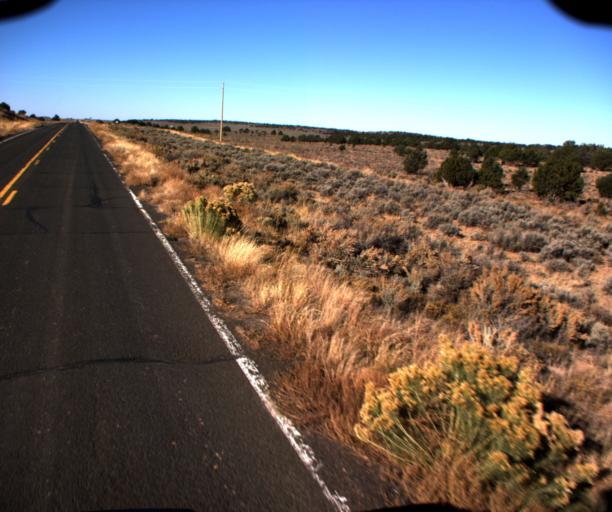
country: US
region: Arizona
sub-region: Navajo County
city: First Mesa
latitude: 35.7641
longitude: -109.9969
